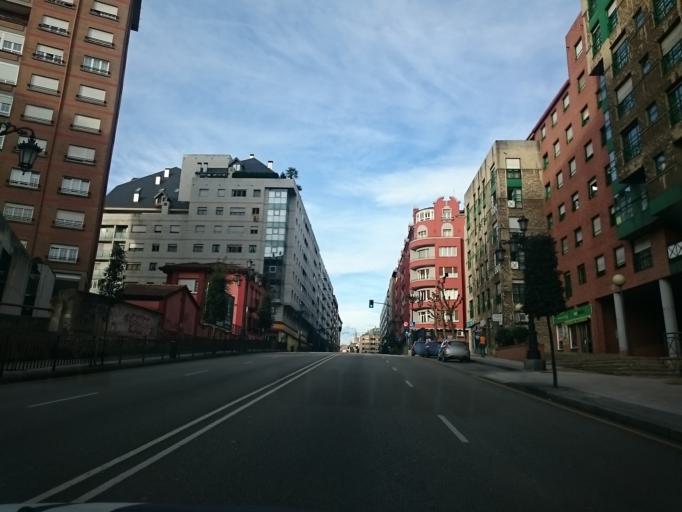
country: ES
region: Asturias
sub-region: Province of Asturias
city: Oviedo
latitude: 43.3556
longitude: -5.8495
